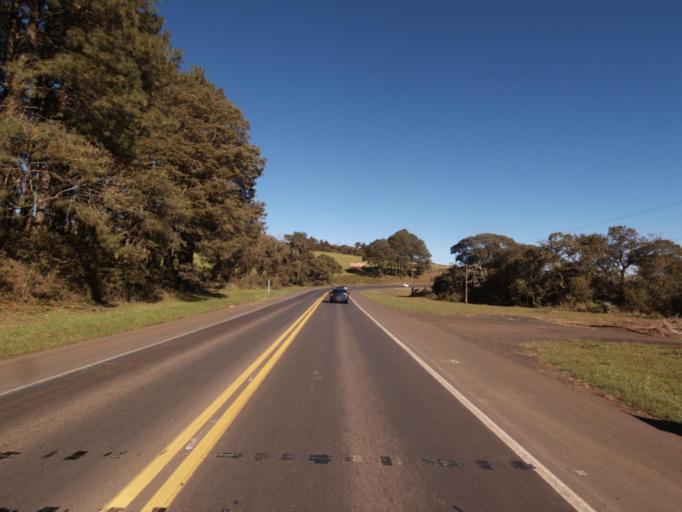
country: BR
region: Santa Catarina
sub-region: Xanxere
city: Xanxere
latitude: -26.9028
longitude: -52.4628
